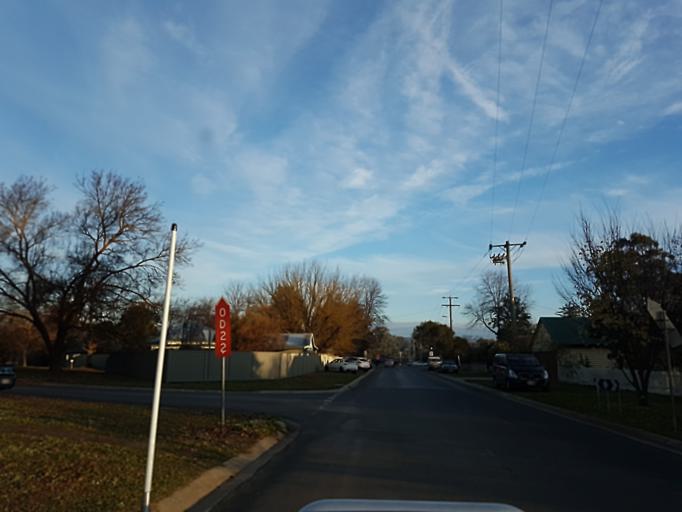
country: AU
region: Victoria
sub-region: Murrindindi
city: Alexandra
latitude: -37.1871
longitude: 145.7063
